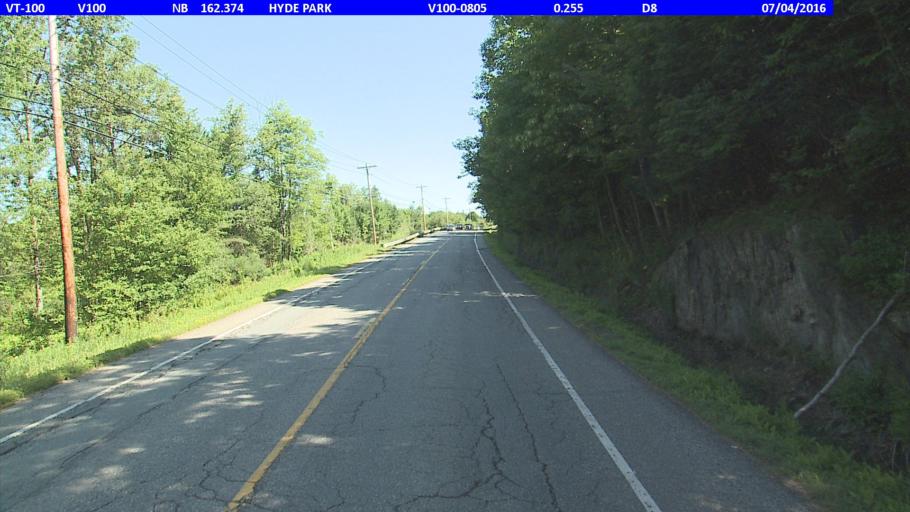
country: US
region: Vermont
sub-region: Lamoille County
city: Hyde Park
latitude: 44.6010
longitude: -72.6151
